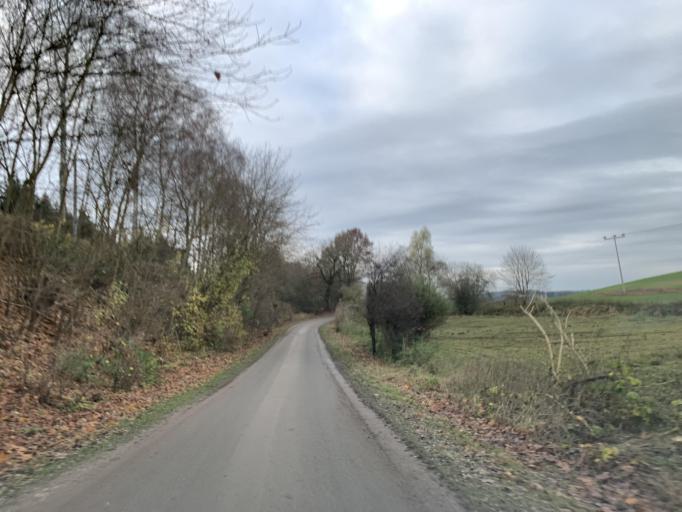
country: DE
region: Mecklenburg-Vorpommern
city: Carpin
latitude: 53.3986
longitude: 13.2150
